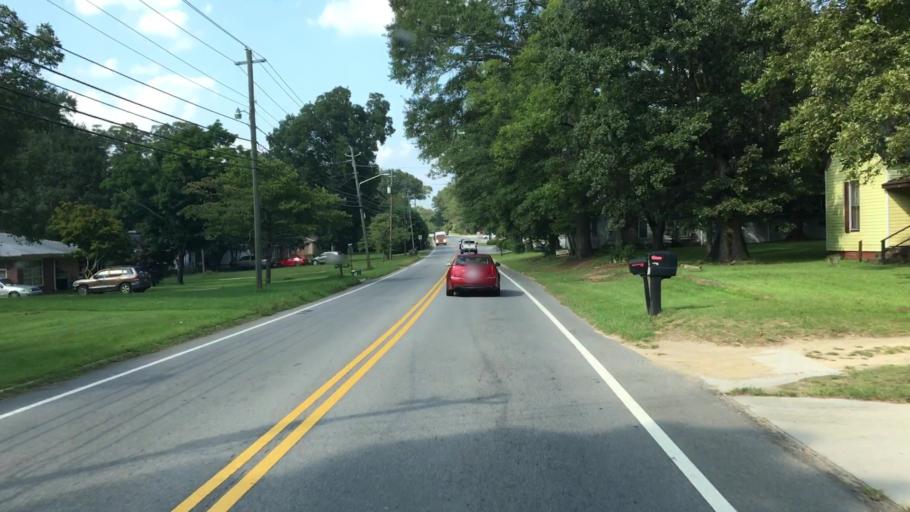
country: US
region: Georgia
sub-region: Walton County
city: Social Circle
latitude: 33.6672
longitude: -83.7115
